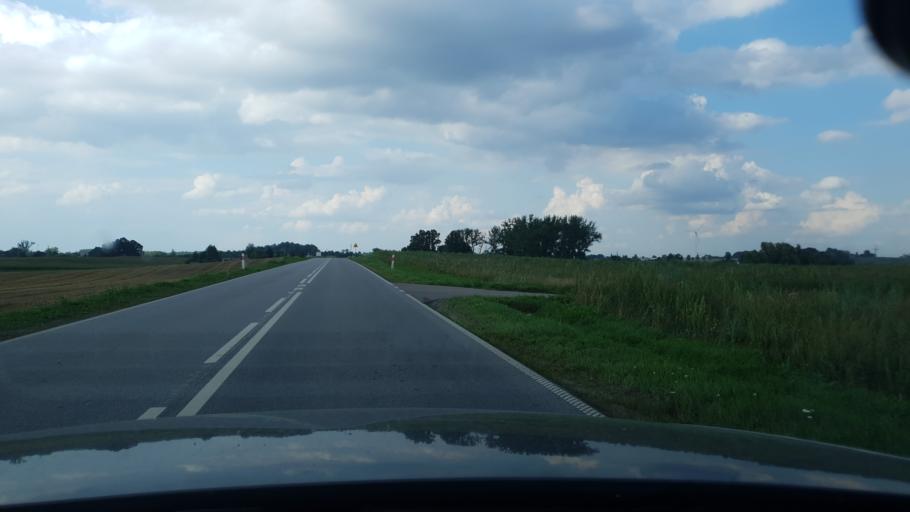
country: PL
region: Kujawsko-Pomorskie
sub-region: Powiat wabrzeski
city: Wabrzezno
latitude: 53.3179
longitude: 18.9356
